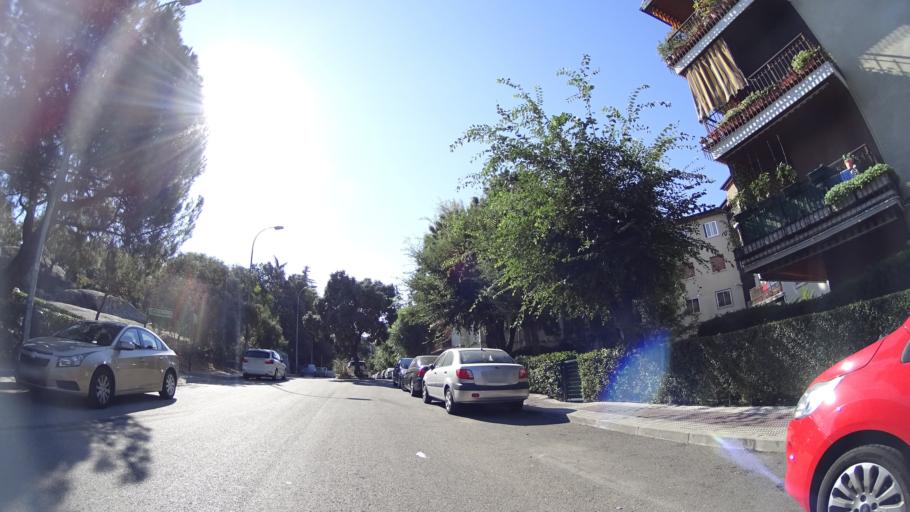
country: ES
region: Madrid
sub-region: Provincia de Madrid
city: Collado-Villalba
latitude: 40.6211
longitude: -4.0041
